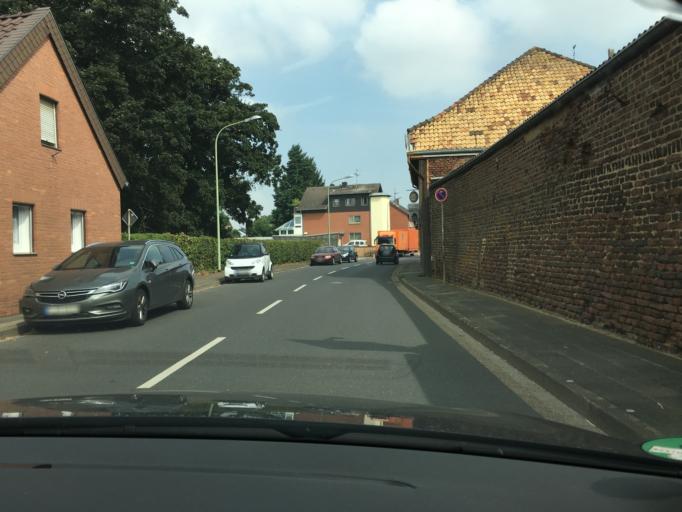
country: DE
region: North Rhine-Westphalia
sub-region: Regierungsbezirk Koln
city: Merzenich
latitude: 50.8377
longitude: 6.5808
